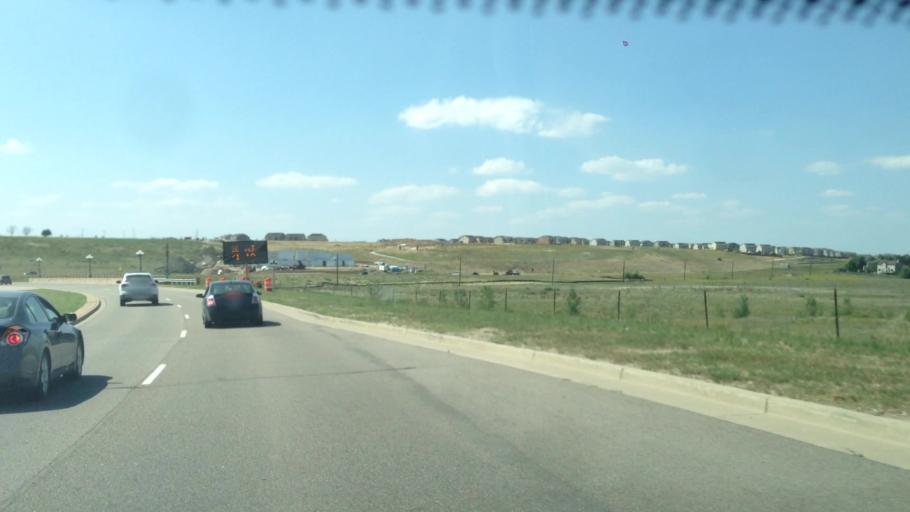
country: US
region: Colorado
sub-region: Douglas County
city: Stonegate
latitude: 39.5164
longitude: -104.8097
